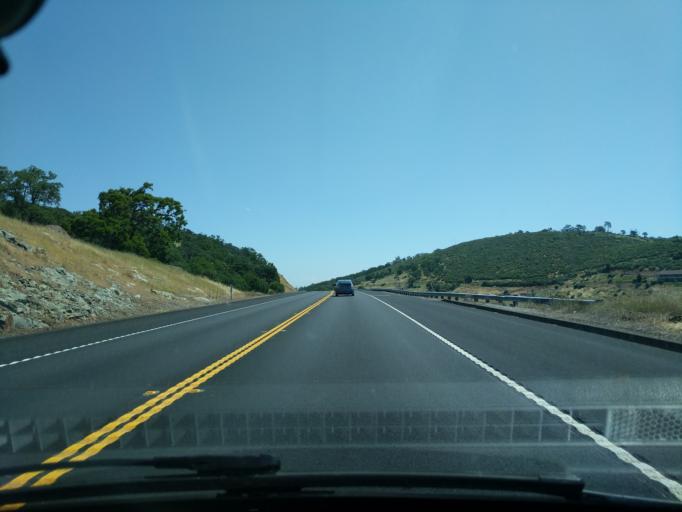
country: US
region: California
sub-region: Calaveras County
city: Copperopolis
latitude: 37.9424
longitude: -120.7080
